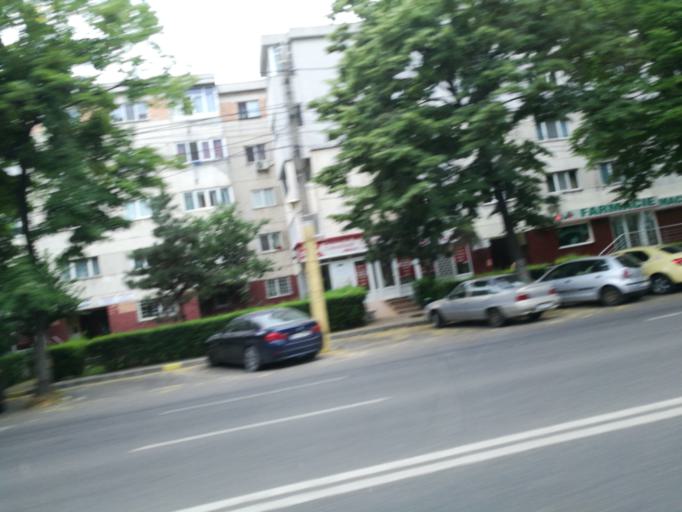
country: RO
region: Constanta
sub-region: Municipiul Constanta
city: Constanta
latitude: 44.1870
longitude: 28.6346
